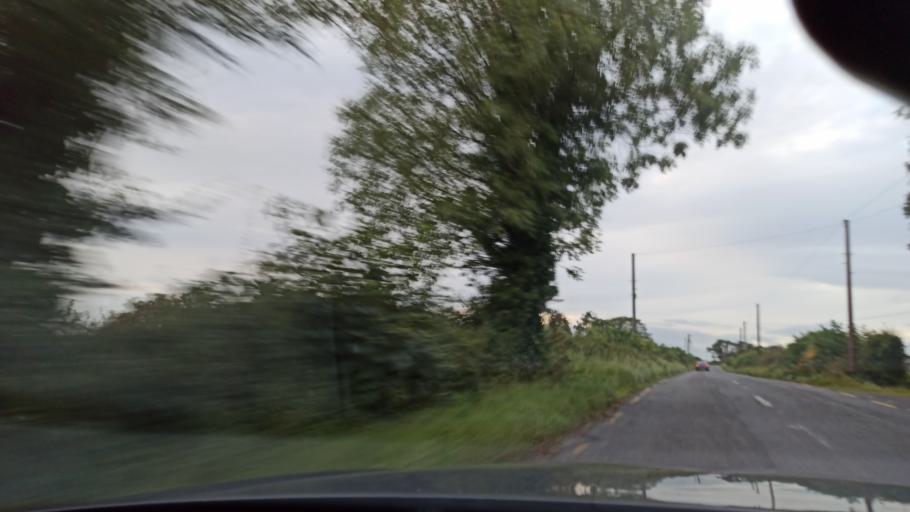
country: IE
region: Munster
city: Cashel
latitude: 52.4951
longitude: -7.8669
